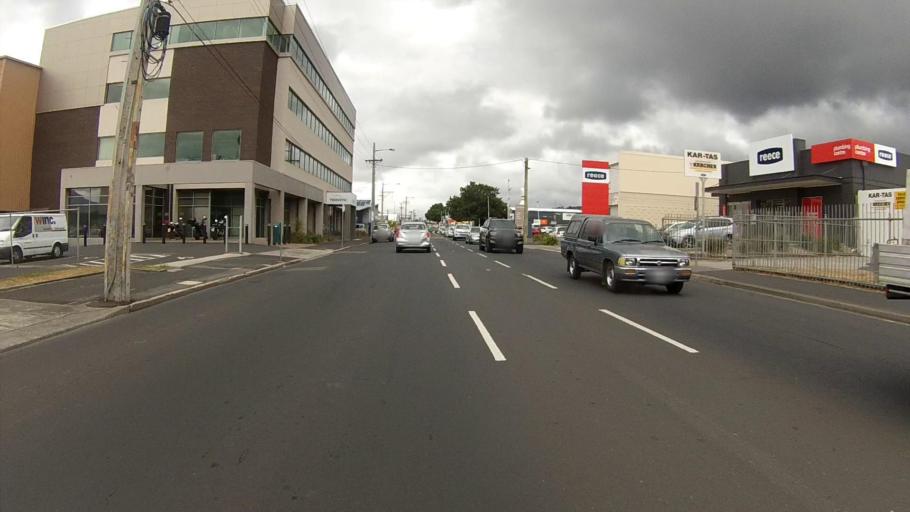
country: AU
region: Tasmania
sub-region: Glenorchy
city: Moonah
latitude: -42.8422
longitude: 147.2917
